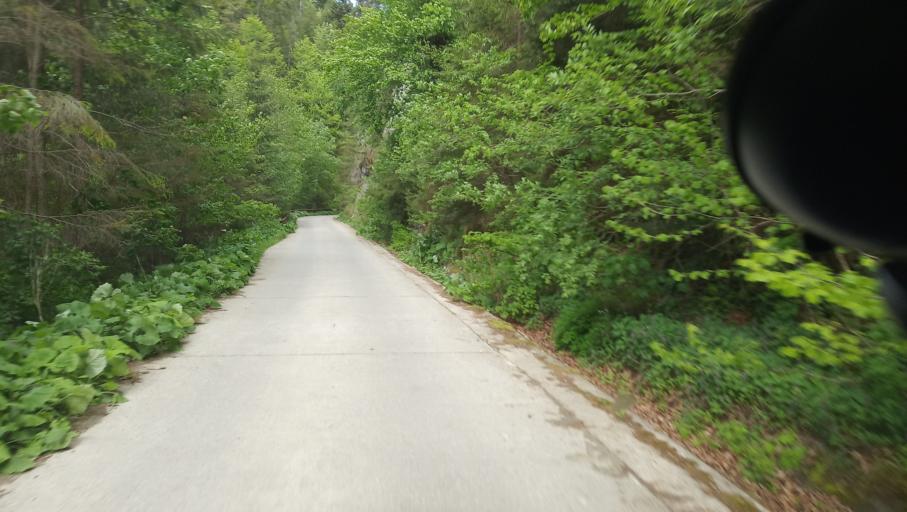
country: RO
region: Alba
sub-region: Comuna Scarisoara
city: Scarisoara
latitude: 46.4629
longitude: 22.8333
